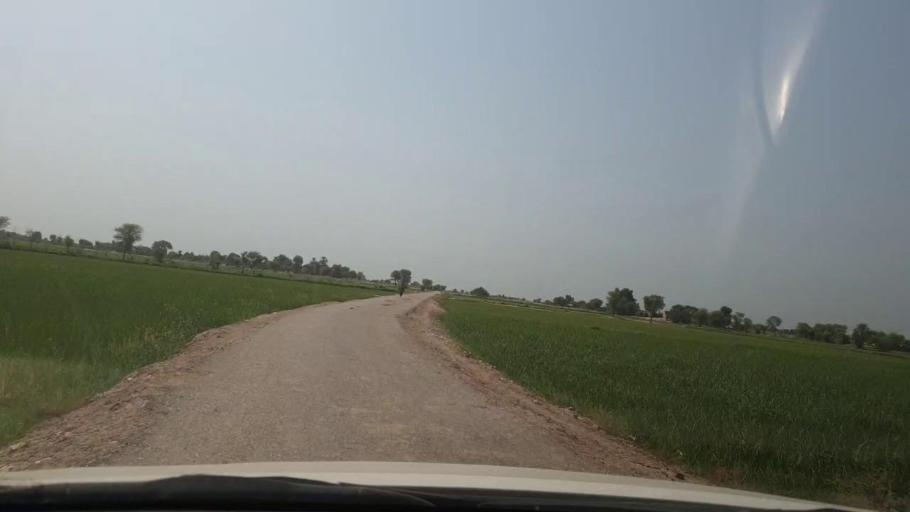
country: PK
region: Sindh
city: Shikarpur
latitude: 28.0044
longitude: 68.7156
